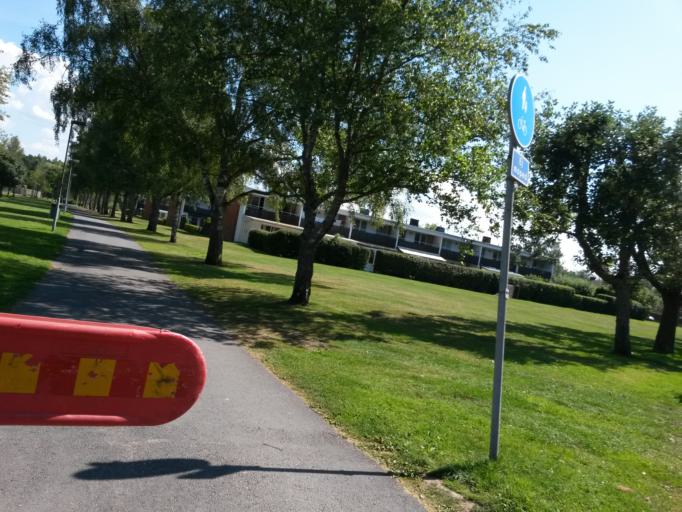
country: SE
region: Vaestra Goetaland
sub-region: Lidkopings Kommun
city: Lidkoping
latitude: 58.4881
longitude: 13.1436
